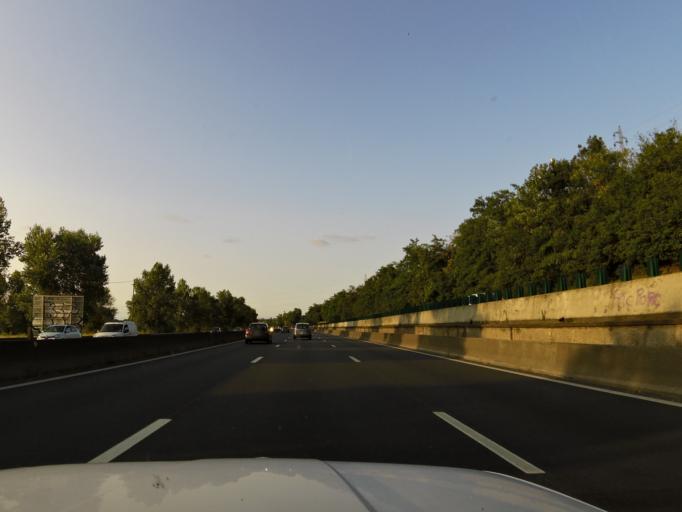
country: FR
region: Rhone-Alpes
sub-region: Departement du Rhone
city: Ternay
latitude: 45.6075
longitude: 4.8028
